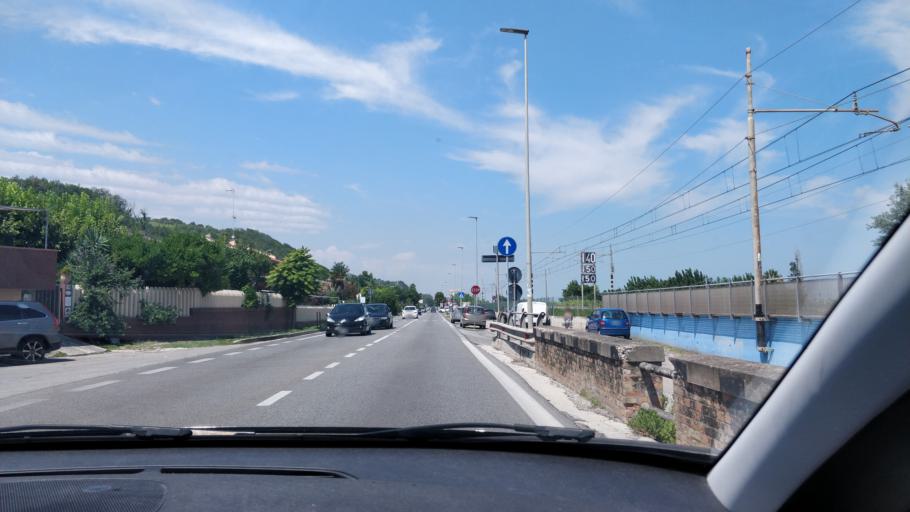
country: IT
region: Abruzzo
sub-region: Provincia di Chieti
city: Tollo
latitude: 42.3806
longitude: 14.3656
